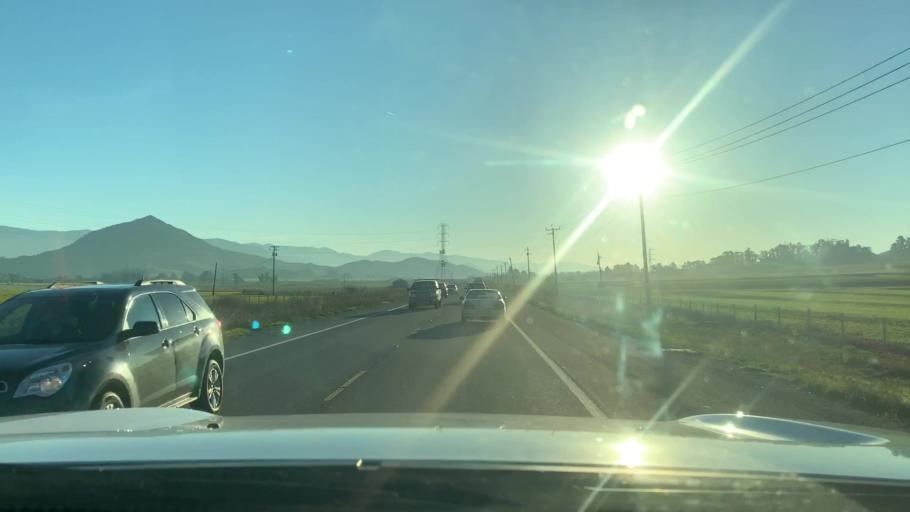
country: US
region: California
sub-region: San Luis Obispo County
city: San Luis Obispo
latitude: 35.2840
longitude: -120.7314
